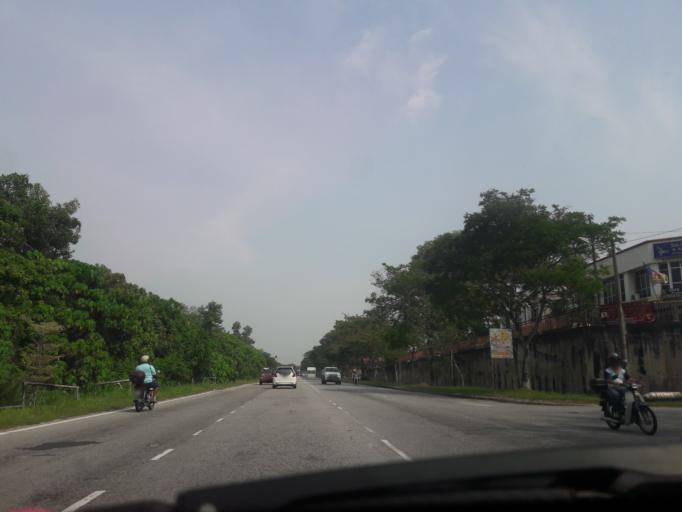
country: MY
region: Kedah
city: Kulim
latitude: 5.3675
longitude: 100.5455
